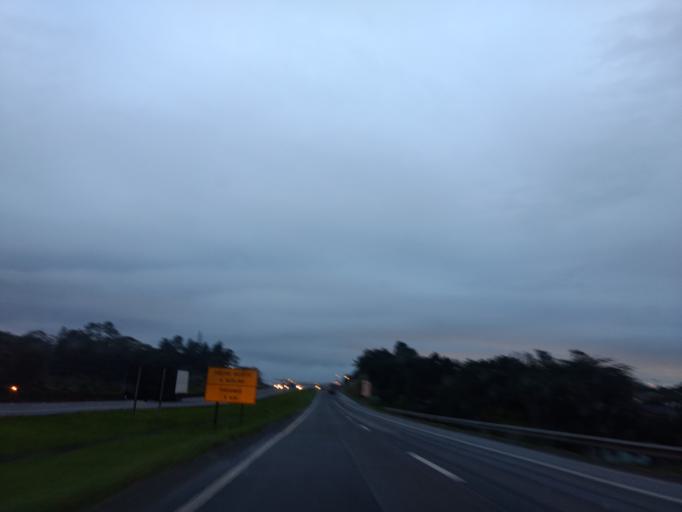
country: BR
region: Sao Paulo
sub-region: Registro
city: Registro
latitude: -24.4647
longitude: -47.8194
